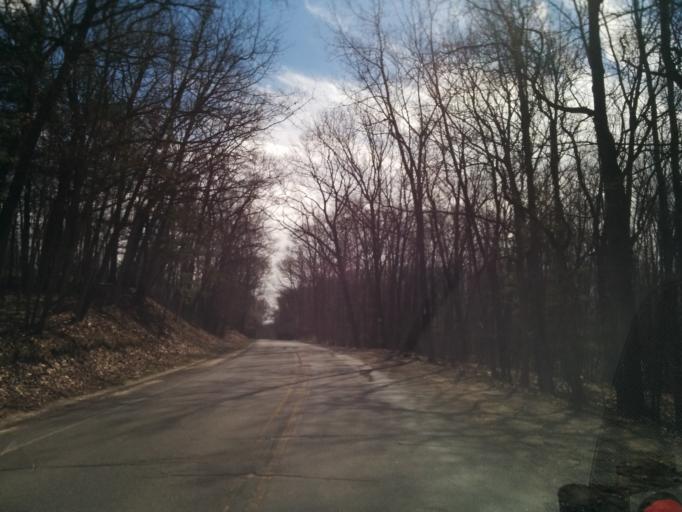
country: US
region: Michigan
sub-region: Newaygo County
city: Newaygo
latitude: 43.4270
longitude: -85.6470
